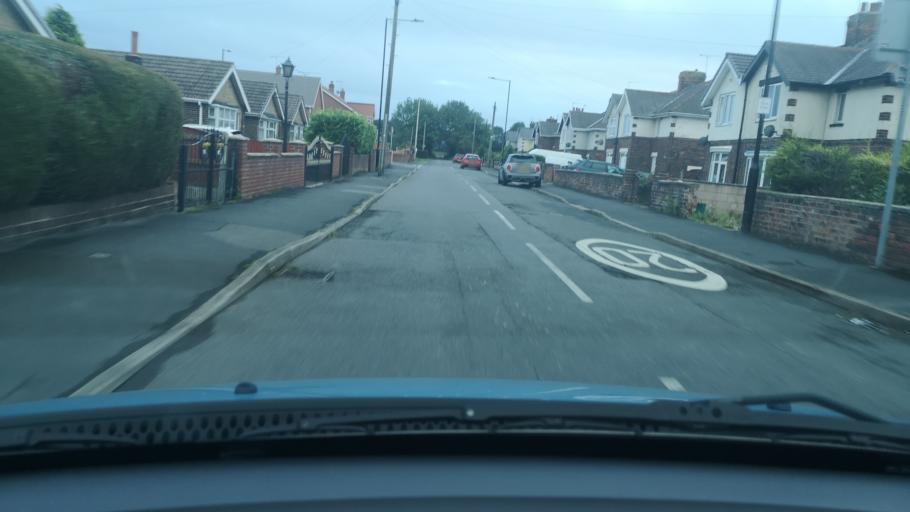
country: GB
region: England
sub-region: Doncaster
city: Askern
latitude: 53.6151
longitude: -1.1416
